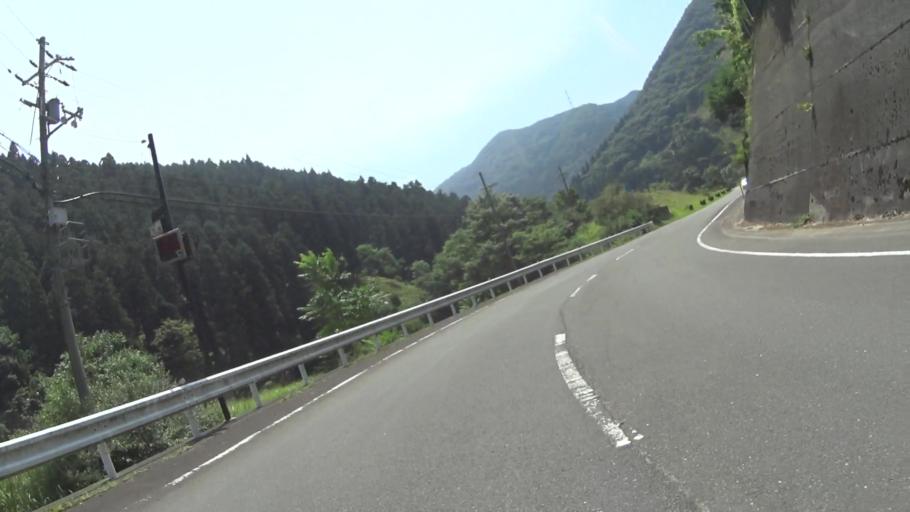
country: JP
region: Kyoto
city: Ayabe
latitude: 35.2944
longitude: 135.4275
